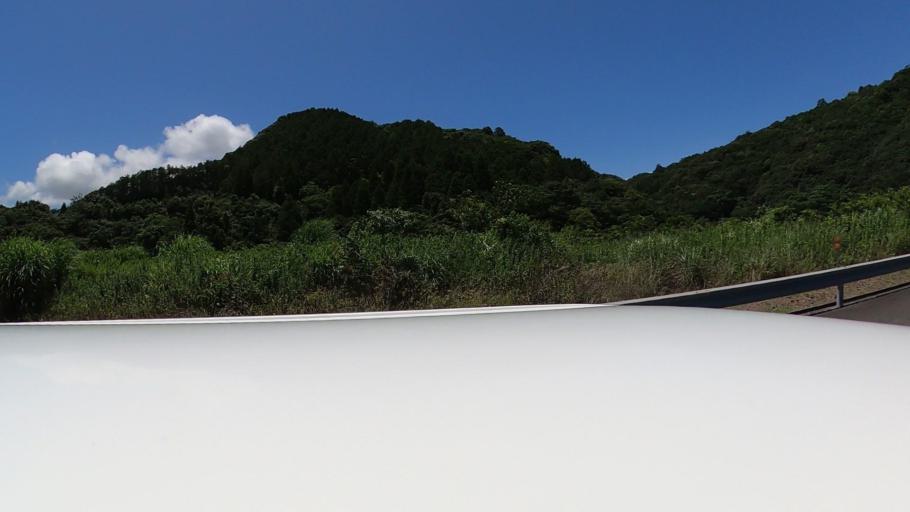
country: JP
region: Miyazaki
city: Nobeoka
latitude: 32.5307
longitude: 131.6647
